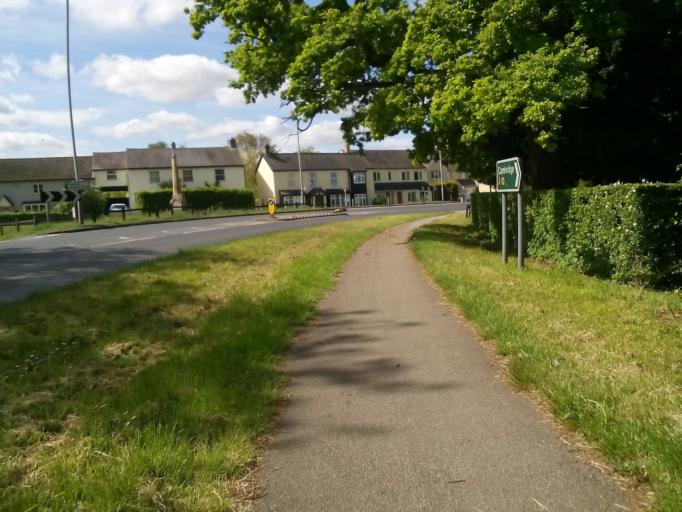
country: GB
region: England
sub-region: Cambridgeshire
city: Harston
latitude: 52.1371
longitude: 0.0803
